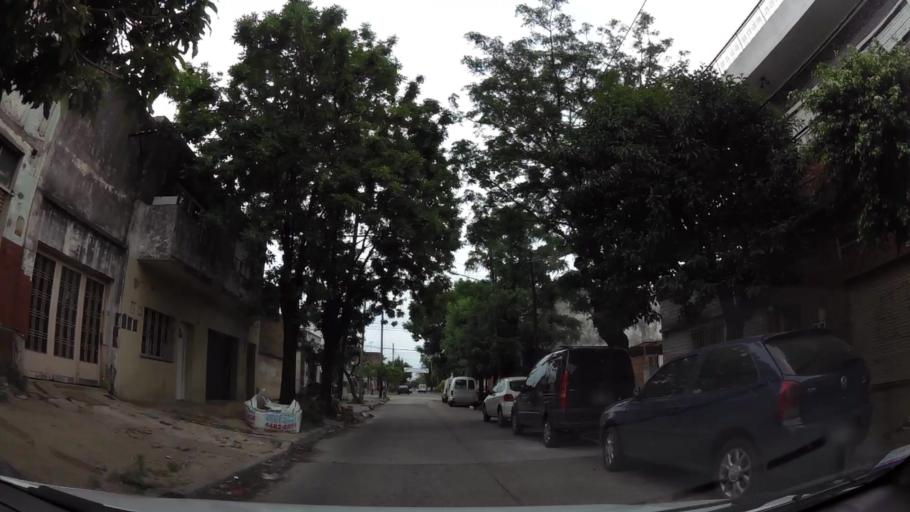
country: AR
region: Buenos Aires F.D.
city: Villa Lugano
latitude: -34.6661
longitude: -58.5152
